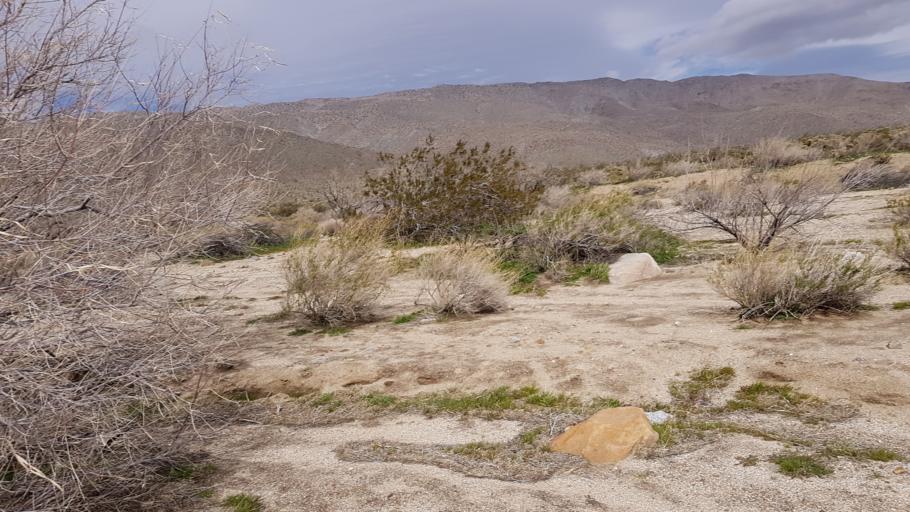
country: US
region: California
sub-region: San Diego County
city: Borrego Springs
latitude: 33.1353
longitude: -116.4355
